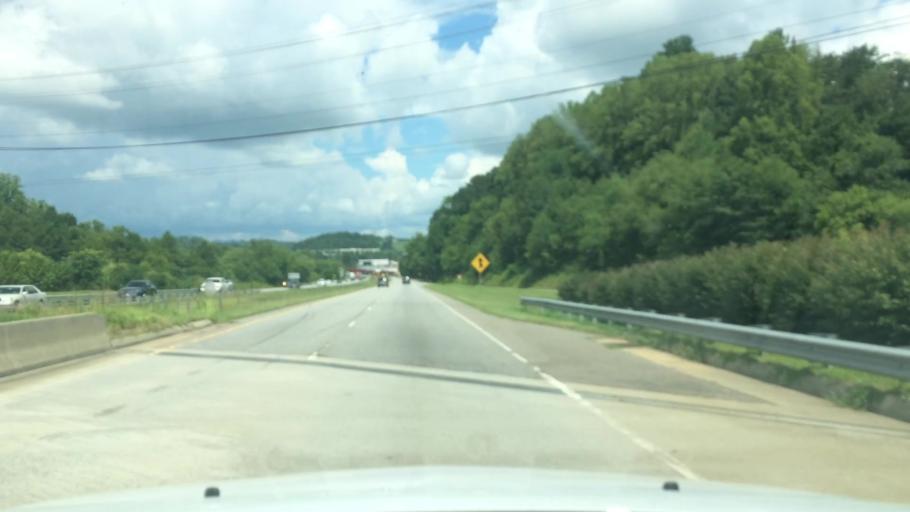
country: US
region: North Carolina
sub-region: Wilkes County
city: Wilkesboro
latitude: 36.1412
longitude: -81.1736
